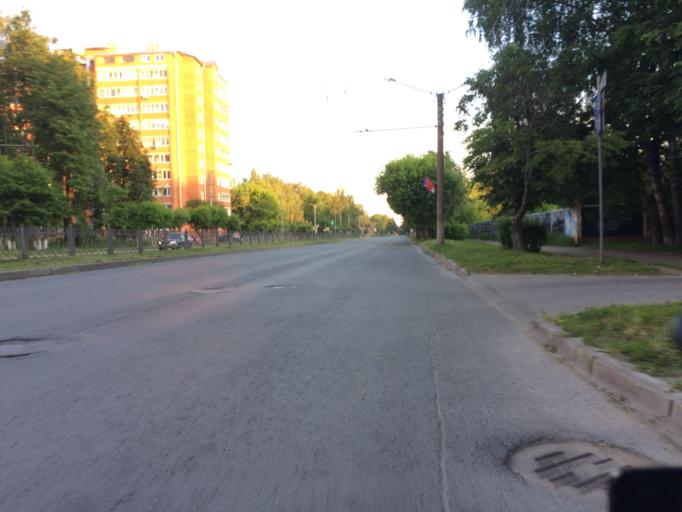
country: RU
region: Mariy-El
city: Yoshkar-Ola
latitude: 56.6434
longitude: 47.8823
